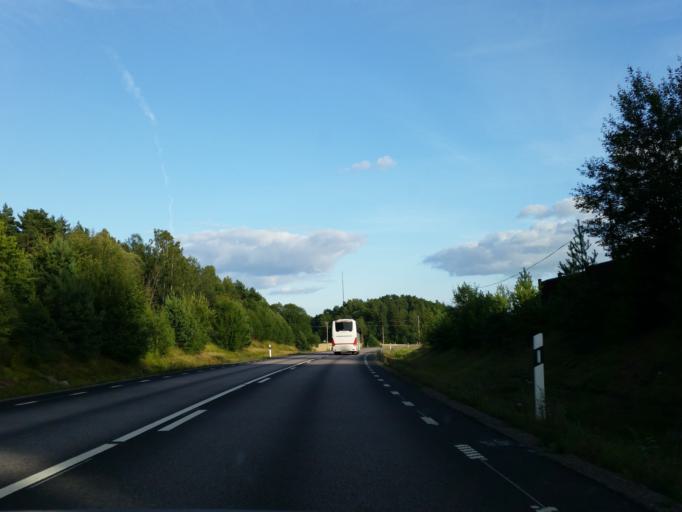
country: SE
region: Soedermanland
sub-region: Gnesta Kommun
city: Gnesta
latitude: 59.0459
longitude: 17.2879
